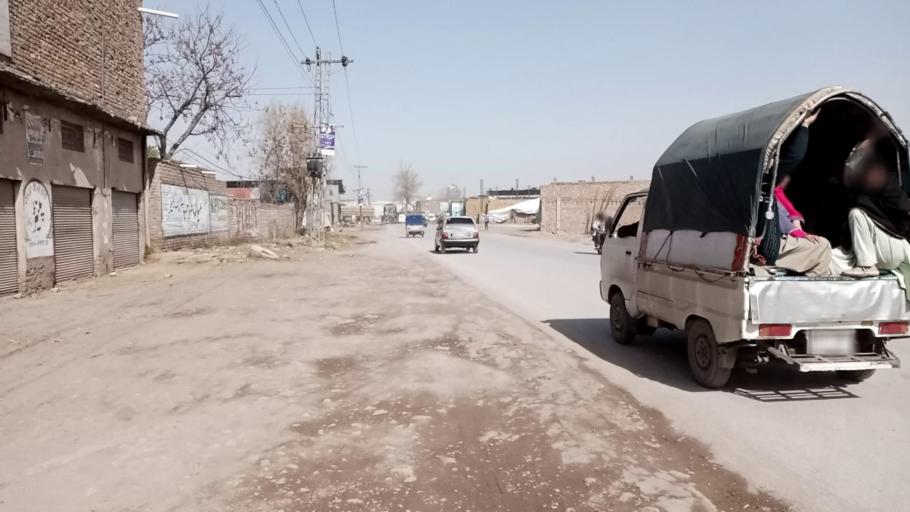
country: PK
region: Khyber Pakhtunkhwa
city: Peshawar
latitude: 34.0164
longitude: 71.6467
